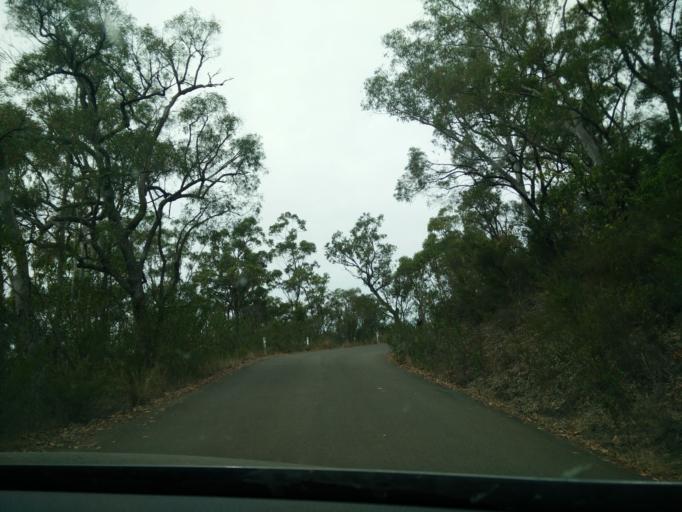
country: AU
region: New South Wales
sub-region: Blue Mountains Municipality
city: Glenbrook
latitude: -33.7808
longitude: 150.6175
